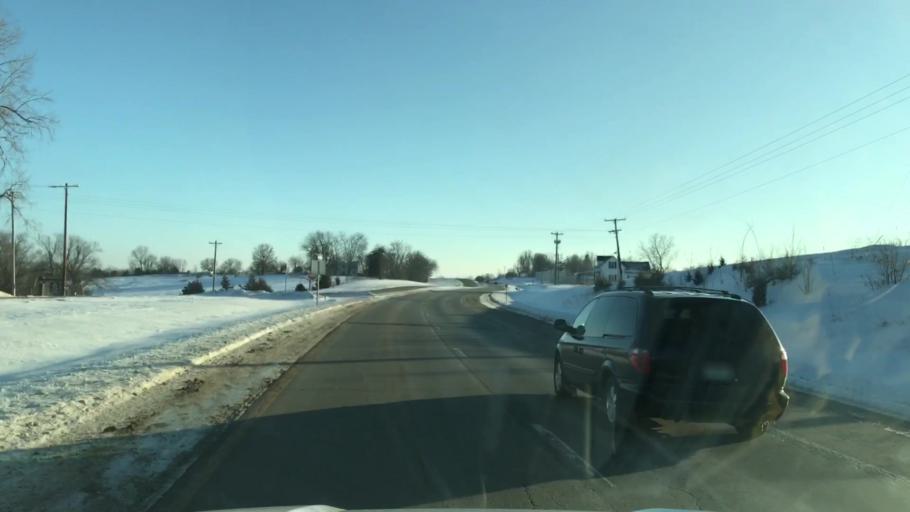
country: US
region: Missouri
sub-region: Andrew County
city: Country Club Village
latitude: 39.8836
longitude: -94.8084
